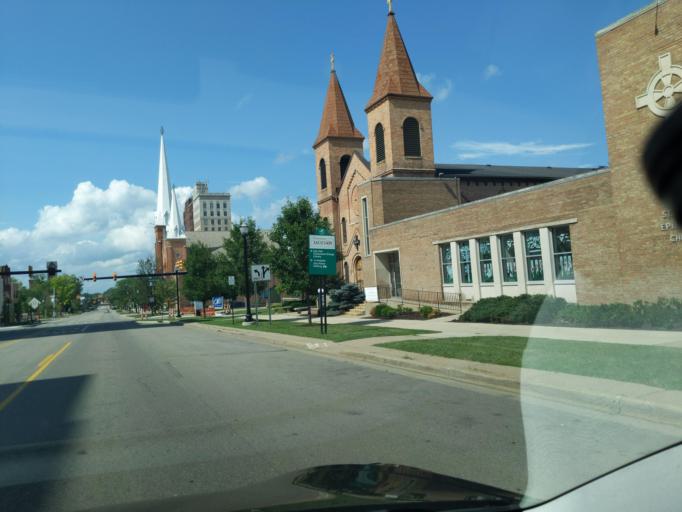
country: US
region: Michigan
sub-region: Jackson County
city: Jackson
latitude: 42.2450
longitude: -84.4088
